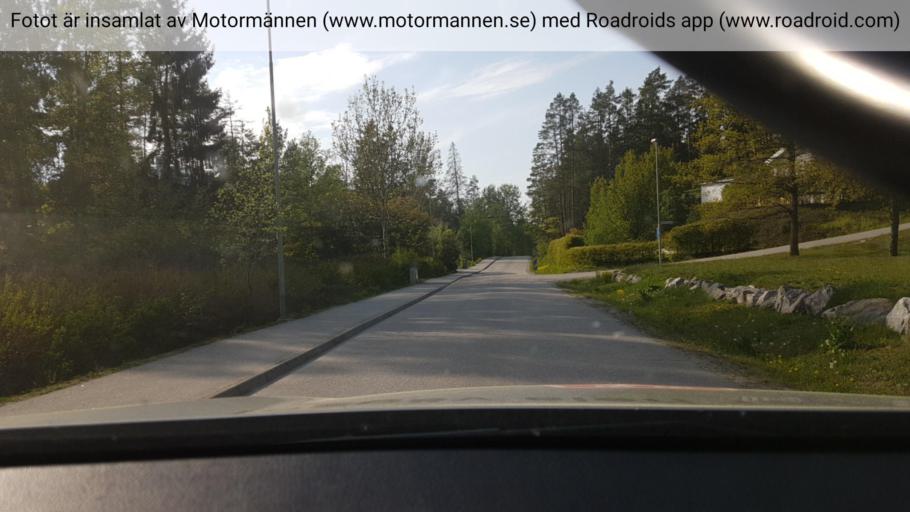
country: SE
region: Stockholm
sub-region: Nacka Kommun
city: Fisksatra
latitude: 59.2496
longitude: 18.2791
